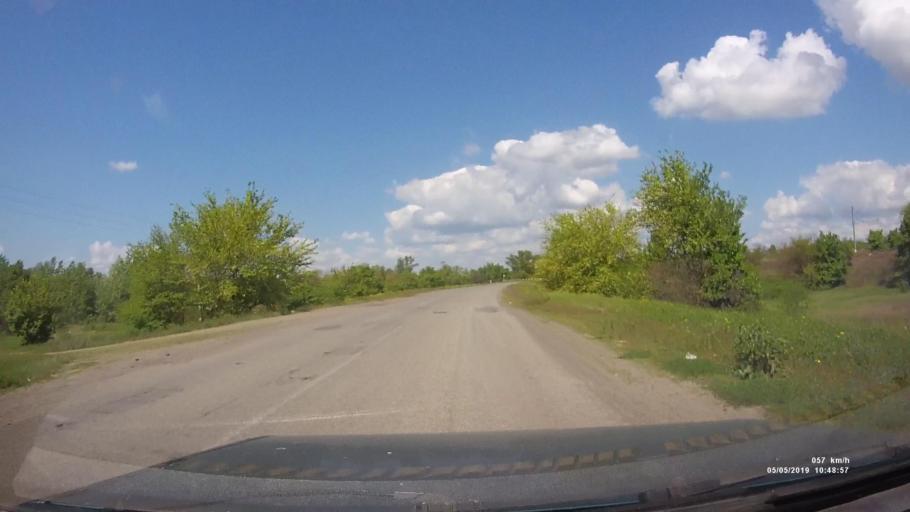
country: RU
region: Rostov
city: Ust'-Donetskiy
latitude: 47.6454
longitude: 40.8133
